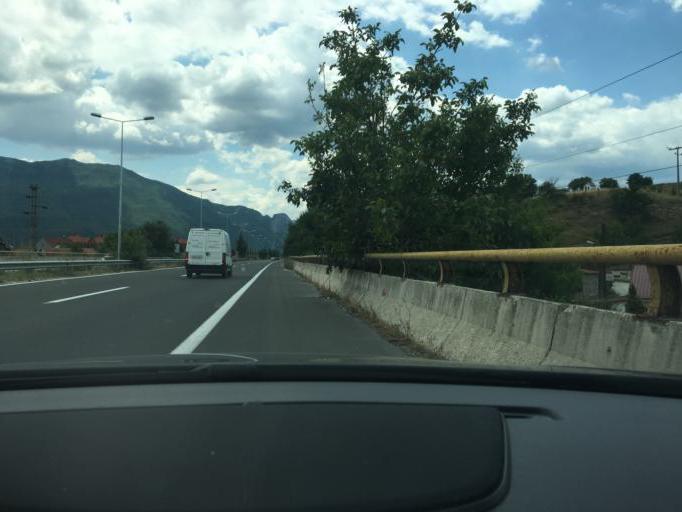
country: MK
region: Saraj
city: Saraj
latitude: 42.0020
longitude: 21.3188
